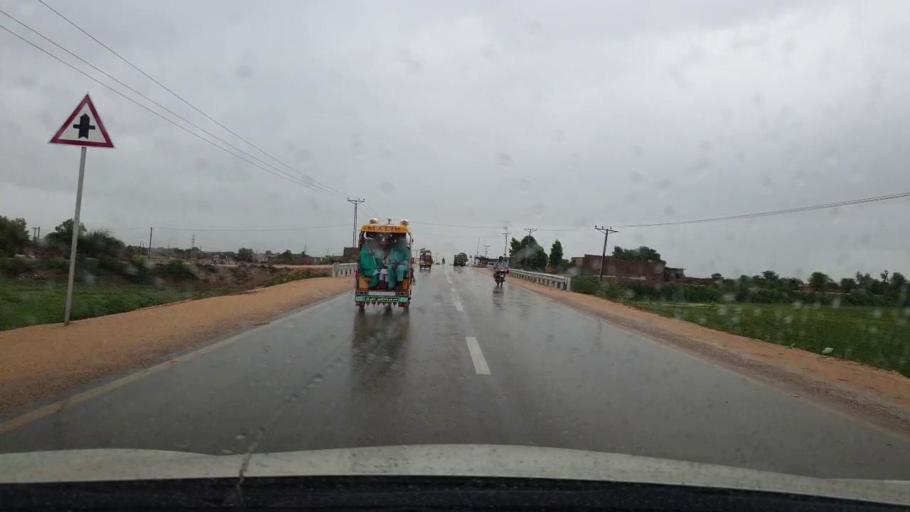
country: PK
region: Sindh
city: Kario
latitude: 24.6536
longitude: 68.5516
